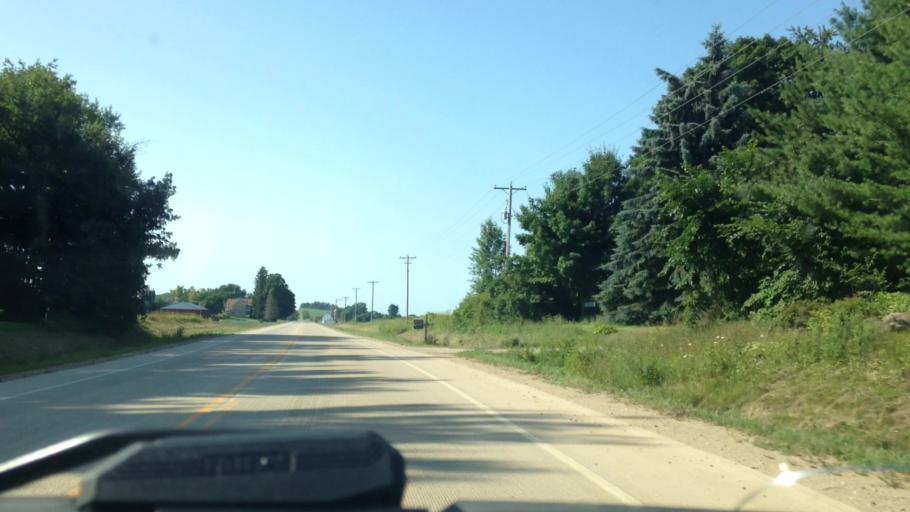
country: US
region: Wisconsin
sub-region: Dodge County
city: Mayville
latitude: 43.4545
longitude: -88.5622
